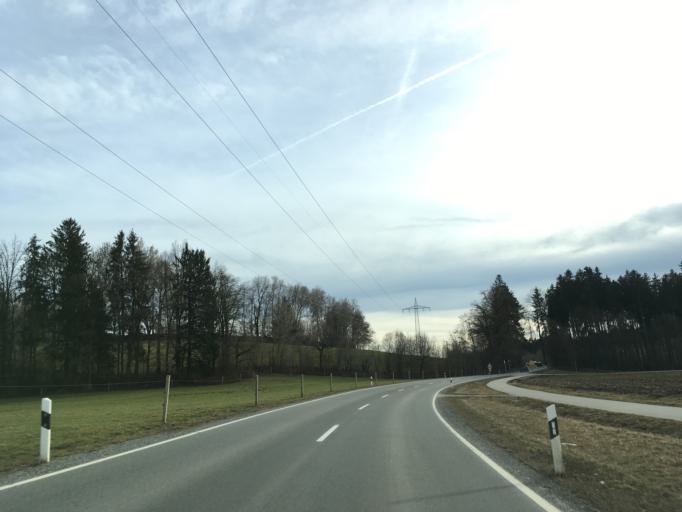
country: DE
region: Bavaria
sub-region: Upper Bavaria
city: Prutting
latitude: 47.9118
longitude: 12.2152
